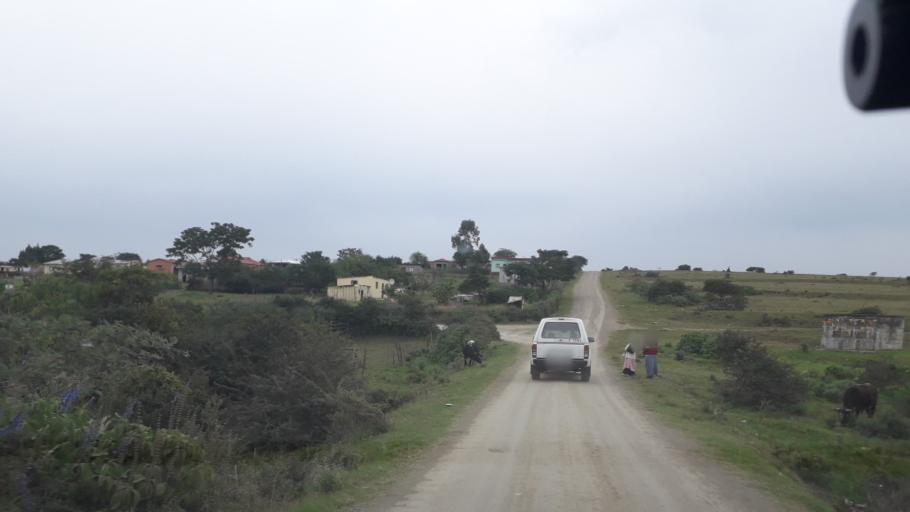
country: ZA
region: Eastern Cape
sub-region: Buffalo City Metropolitan Municipality
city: Bhisho
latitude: -32.7960
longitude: 27.3430
